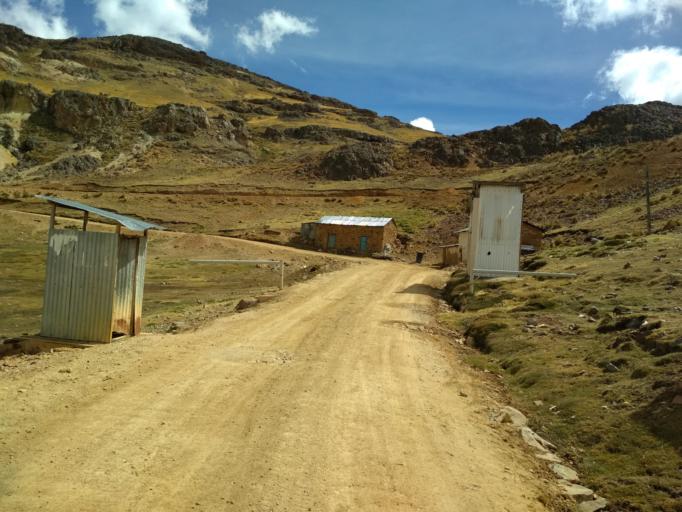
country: PE
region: Huancavelica
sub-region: Provincia de Huancavelica
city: Acobambilla
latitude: -12.6370
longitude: -75.5326
